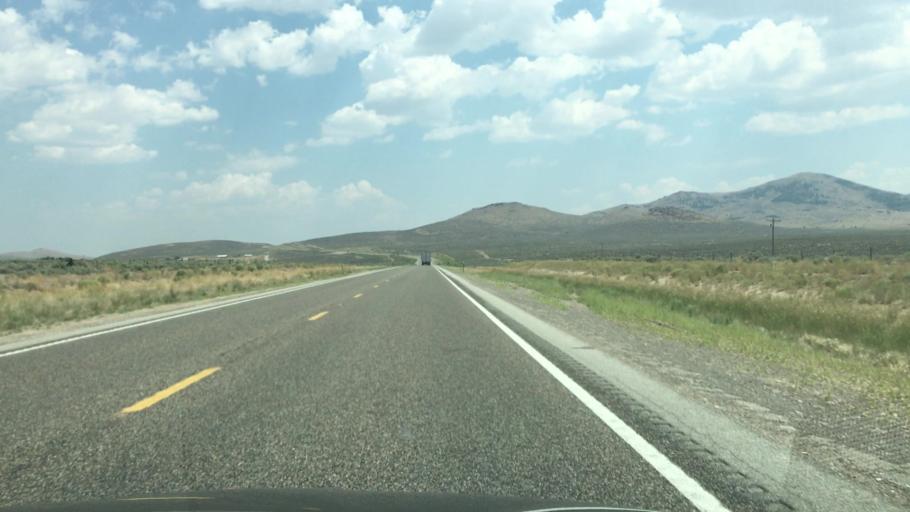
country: US
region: Nevada
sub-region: Elko County
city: Wells
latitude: 41.1659
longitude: -114.8878
